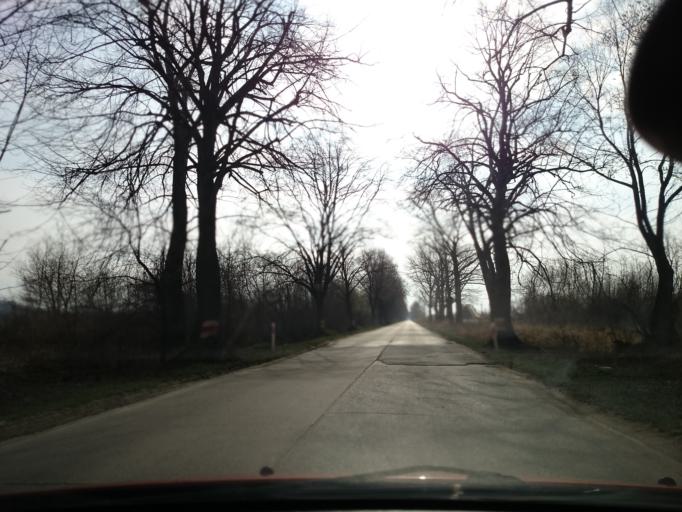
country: PL
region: Opole Voivodeship
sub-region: Powiat nyski
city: Kamienica
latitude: 50.4933
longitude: 16.9645
